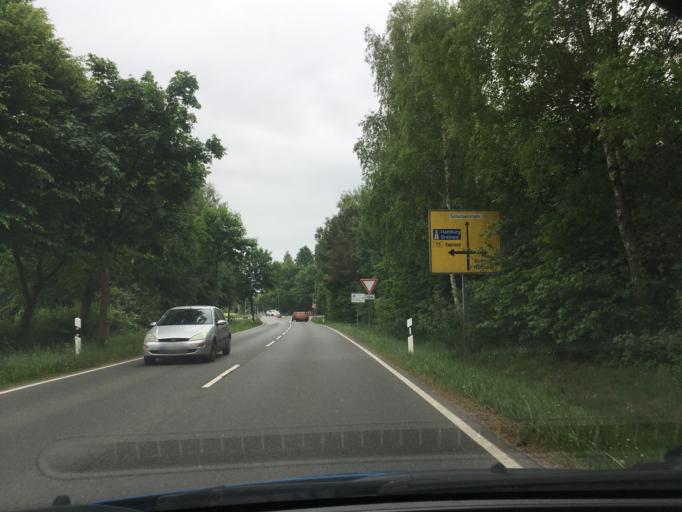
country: DE
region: Lower Saxony
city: Buchholz in der Nordheide
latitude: 53.3452
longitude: 9.8793
